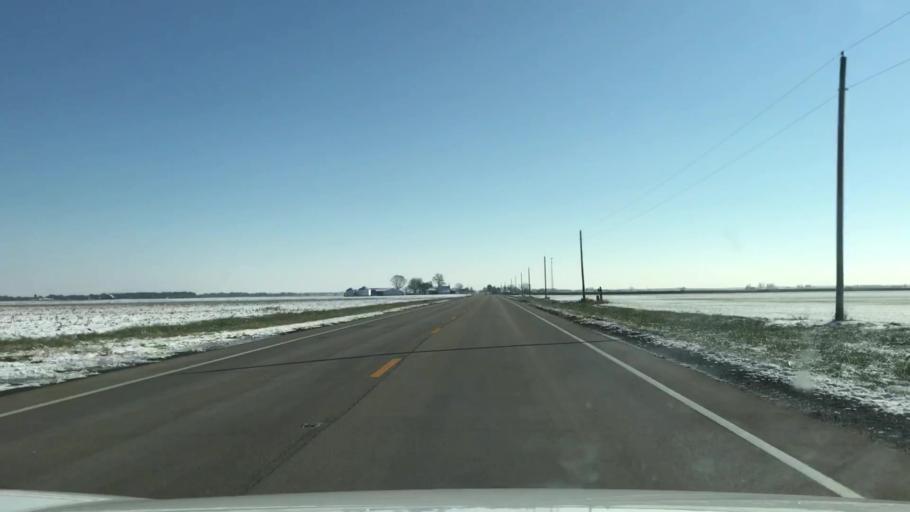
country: US
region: Illinois
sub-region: Washington County
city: Okawville
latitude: 38.4427
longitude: -89.5183
